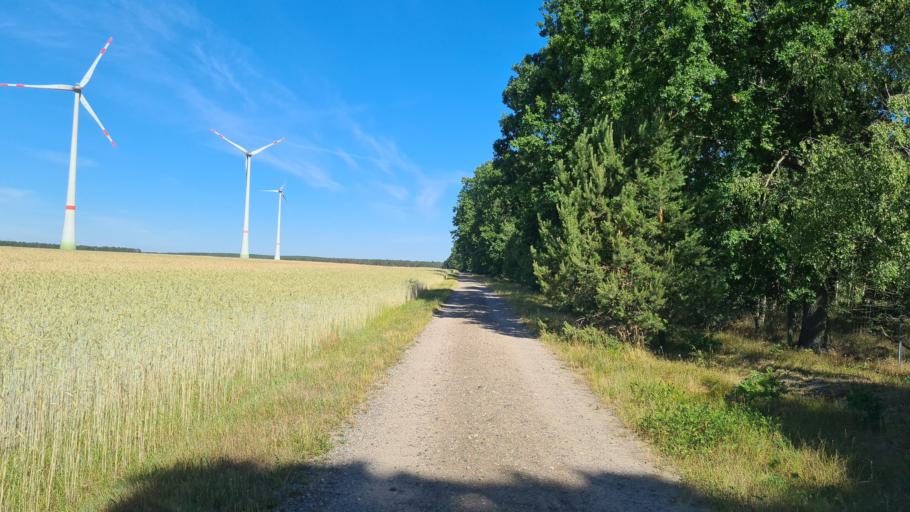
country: DE
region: Brandenburg
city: Treuenbrietzen
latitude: 52.0252
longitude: 12.8599
